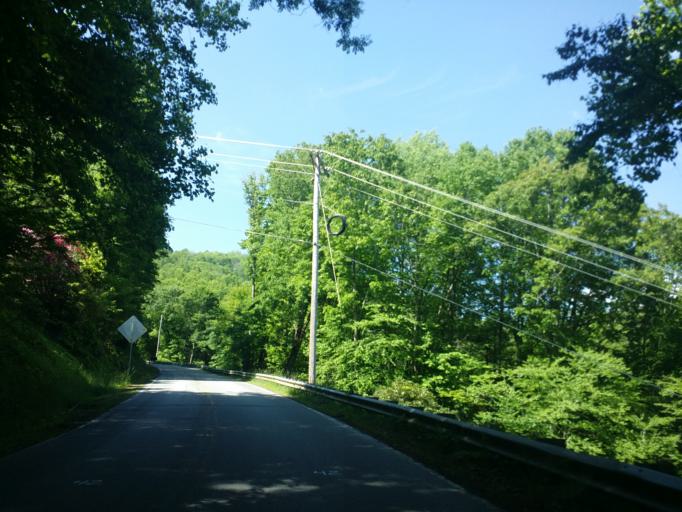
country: US
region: North Carolina
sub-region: Madison County
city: Marshall
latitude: 35.7204
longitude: -82.8395
